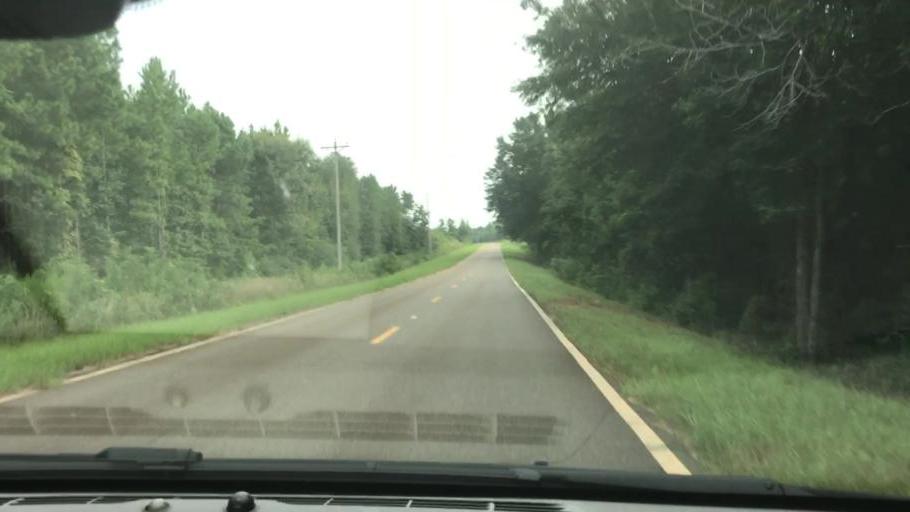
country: US
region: Georgia
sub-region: Stewart County
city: Lumpkin
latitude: 32.0340
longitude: -84.9106
